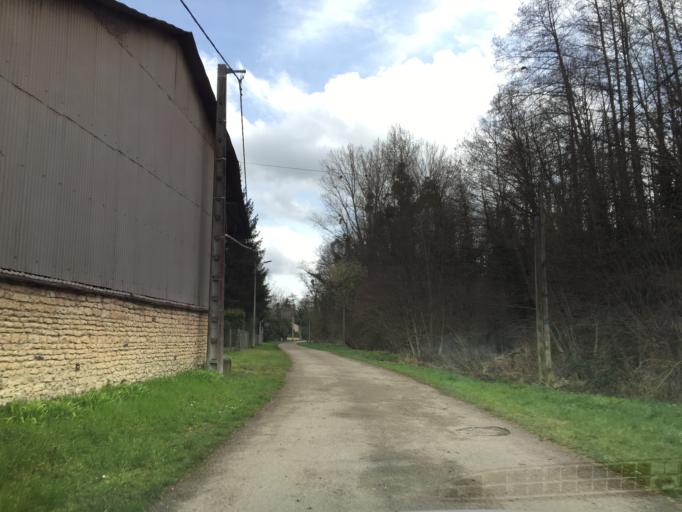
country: FR
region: Bourgogne
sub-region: Departement de l'Yonne
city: Fleury-la-Vallee
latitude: 47.8454
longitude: 3.3994
